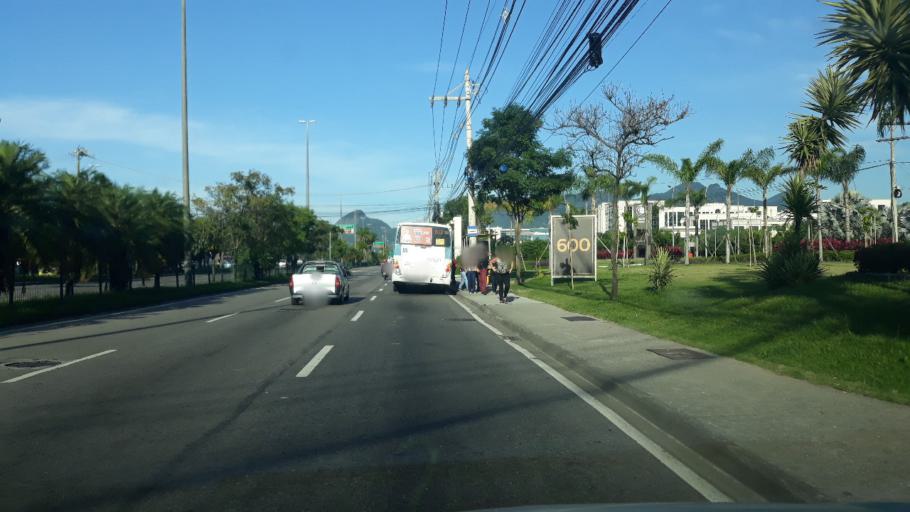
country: BR
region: Rio de Janeiro
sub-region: Sao Joao De Meriti
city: Sao Joao de Meriti
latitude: -22.9731
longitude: -43.3666
